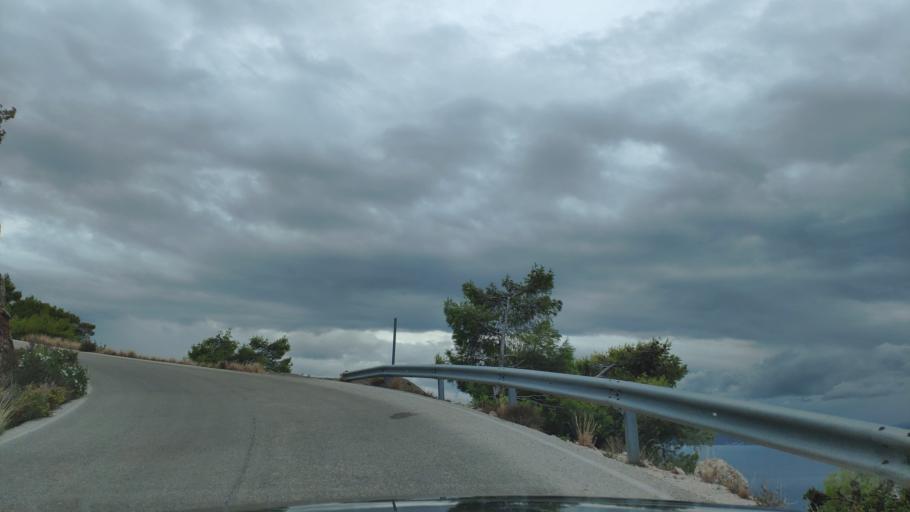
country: GR
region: Peloponnese
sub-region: Nomos Korinthias
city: Perachora
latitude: 38.0043
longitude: 22.9329
